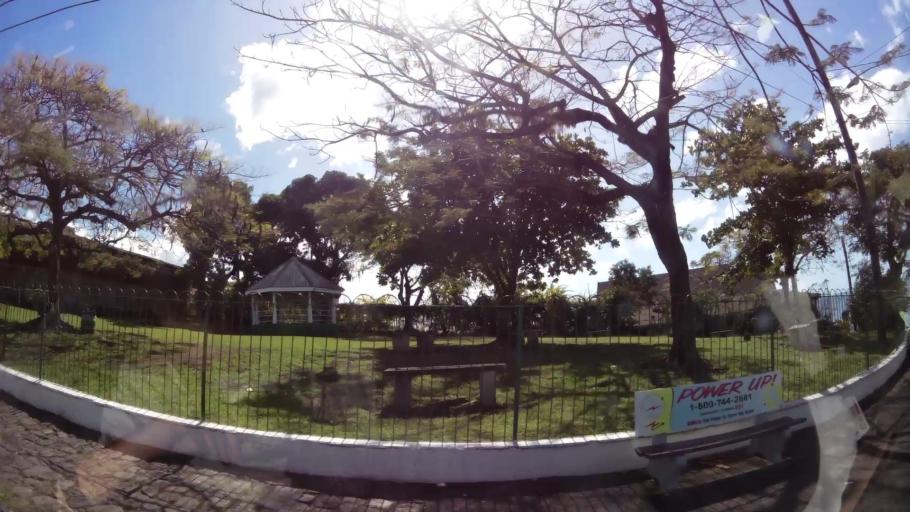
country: DM
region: Saint George
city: Roseau
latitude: 15.2962
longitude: -61.3867
